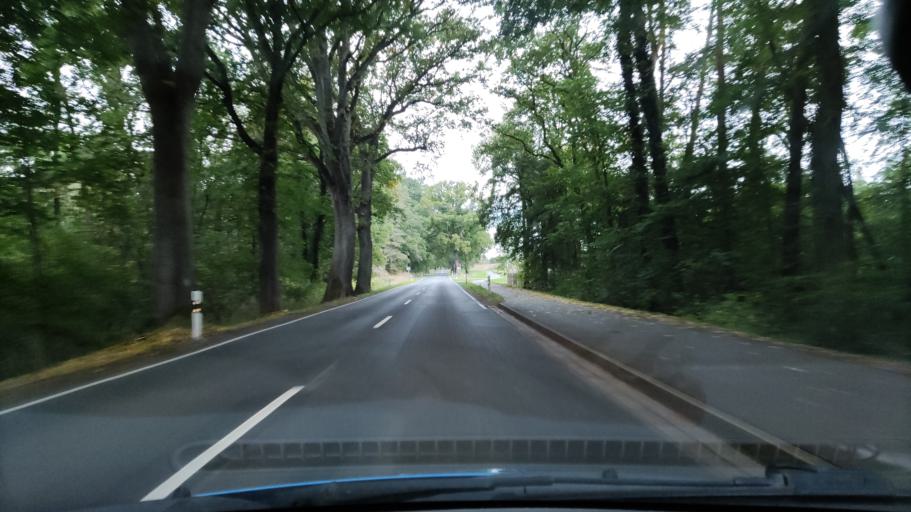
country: DE
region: Mecklenburg-Vorpommern
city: Lubtheen
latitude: 53.3855
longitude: 10.9667
